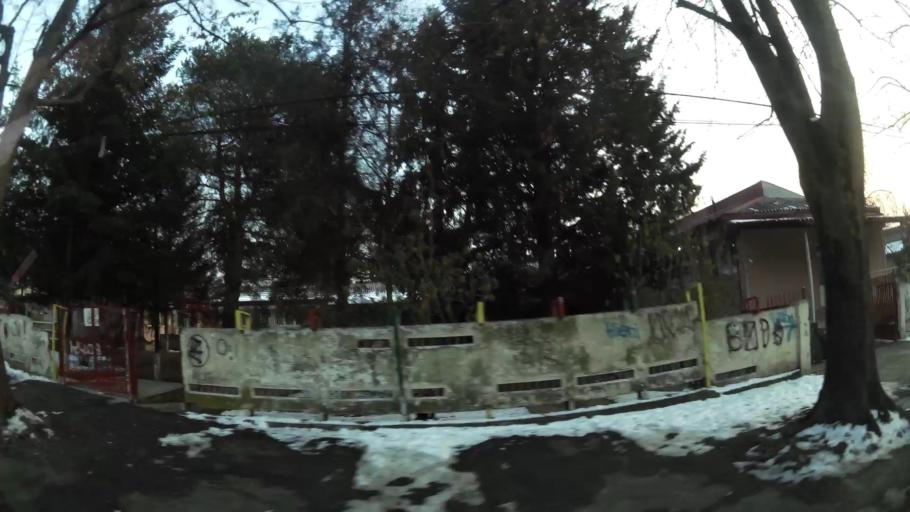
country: MK
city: Creshevo
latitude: 42.0097
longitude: 21.5040
